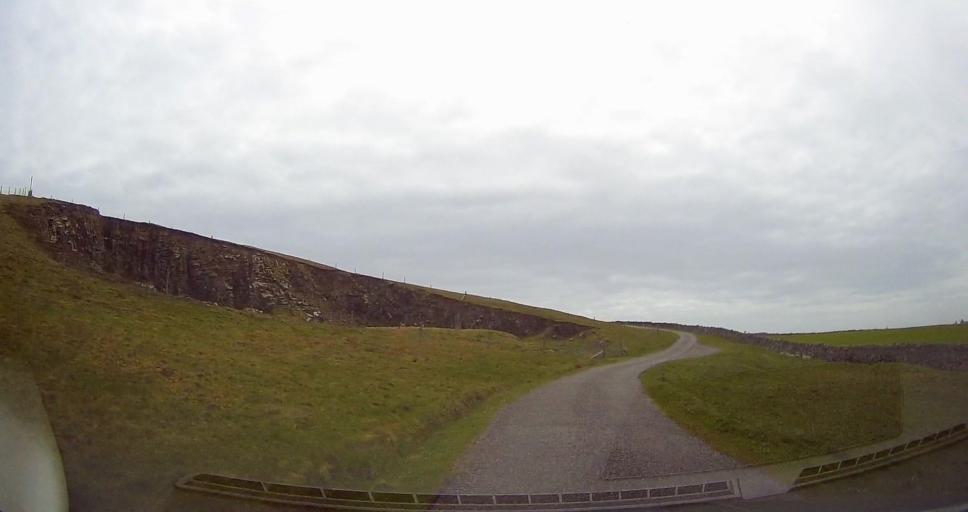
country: GB
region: Scotland
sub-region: Shetland Islands
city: Sandwick
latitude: 59.8720
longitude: -1.2768
